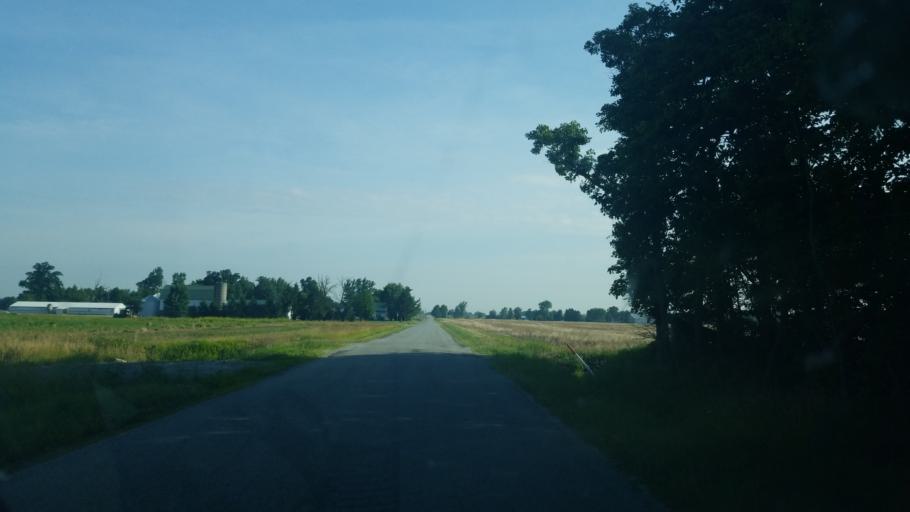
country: US
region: Ohio
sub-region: Hancock County
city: Arlington
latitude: 40.7976
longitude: -83.6707
